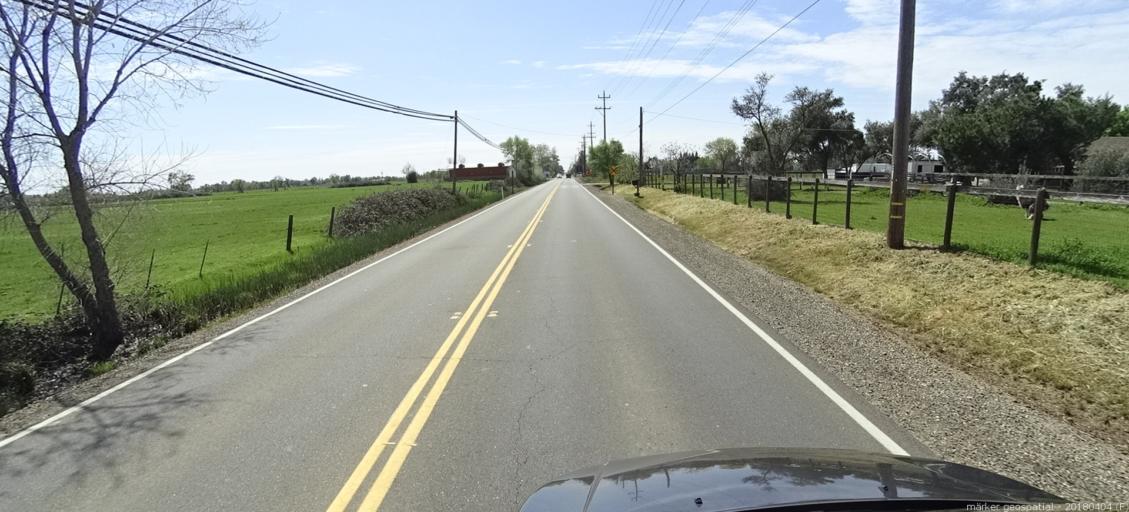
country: US
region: California
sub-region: Sacramento County
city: Wilton
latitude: 38.4031
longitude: -121.2541
